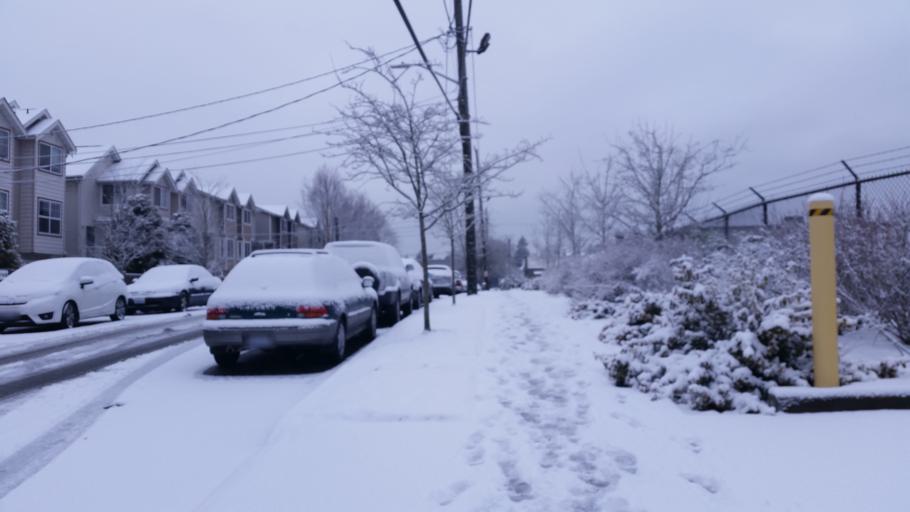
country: US
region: Washington
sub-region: King County
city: Shoreline
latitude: 47.6972
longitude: -122.3423
